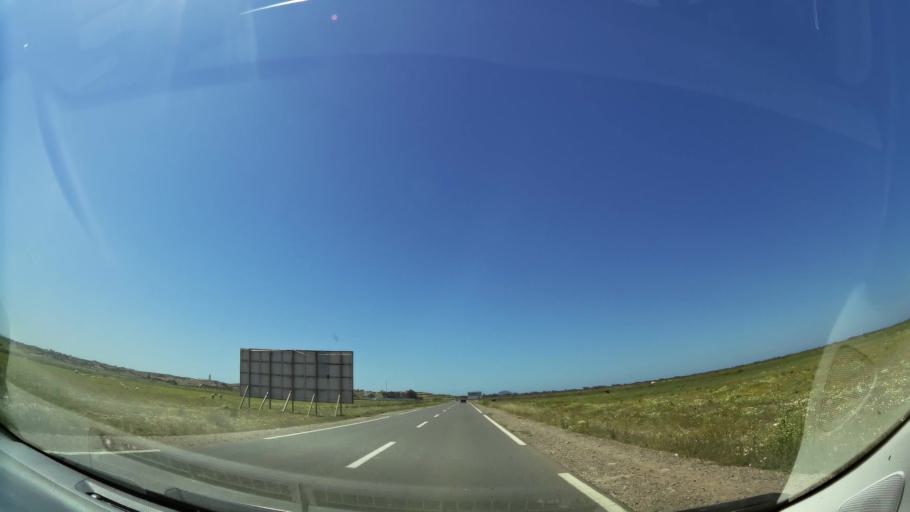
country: MA
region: Oriental
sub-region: Berkane-Taourirt
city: Madagh
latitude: 35.1161
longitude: -2.3684
